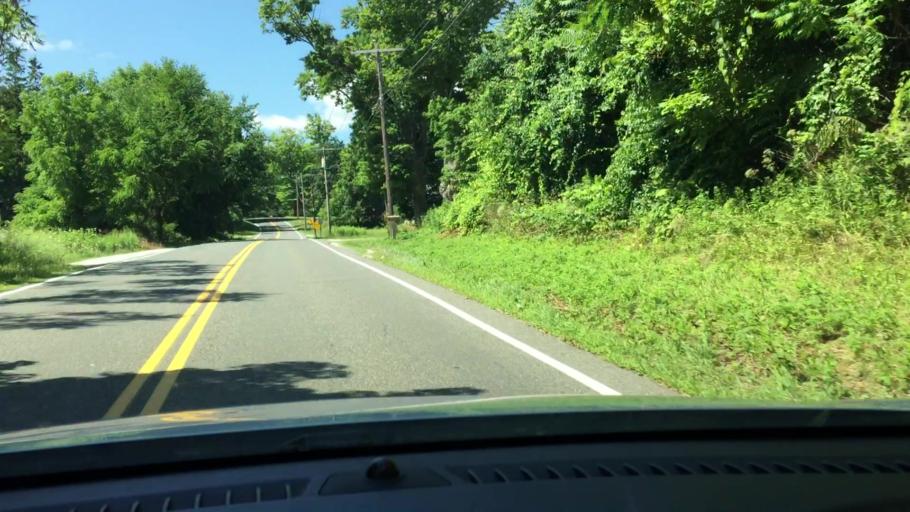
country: US
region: Massachusetts
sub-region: Berkshire County
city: Lenox
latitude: 42.3742
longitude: -73.2577
